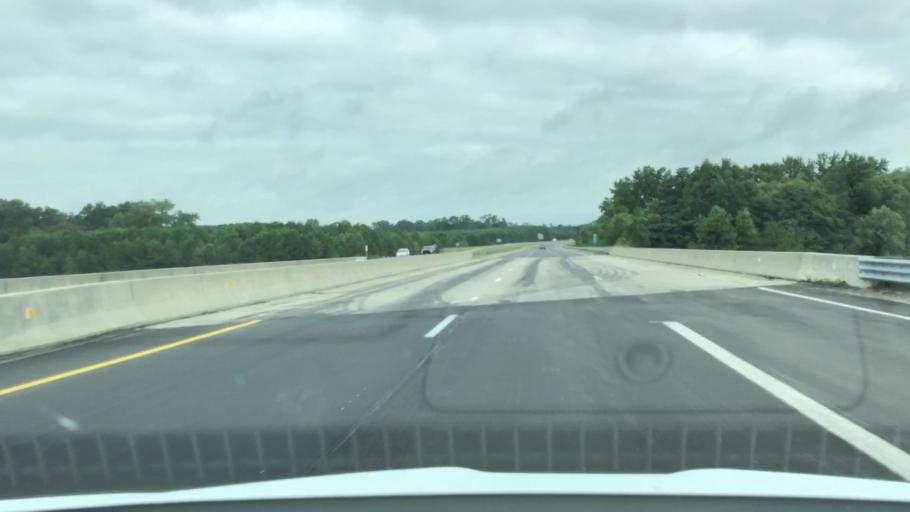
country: US
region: North Carolina
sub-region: Wilson County
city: Lucama
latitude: 35.6694
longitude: -77.9578
